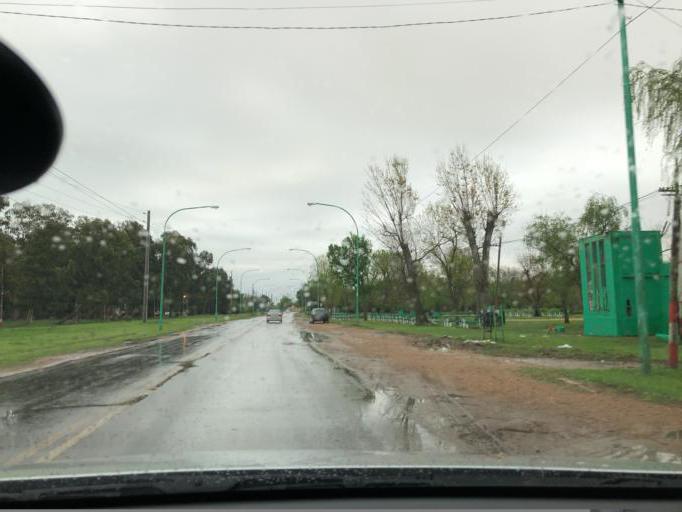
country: AR
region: Buenos Aires
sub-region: Partido de Ensenada
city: Ensenada
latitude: -34.8325
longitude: -57.9515
